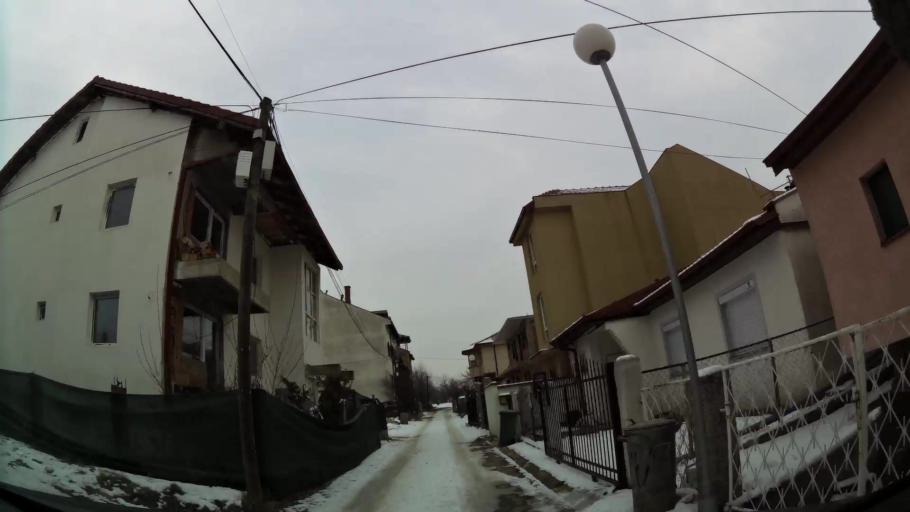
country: MK
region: Butel
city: Butel
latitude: 42.0354
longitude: 21.4500
